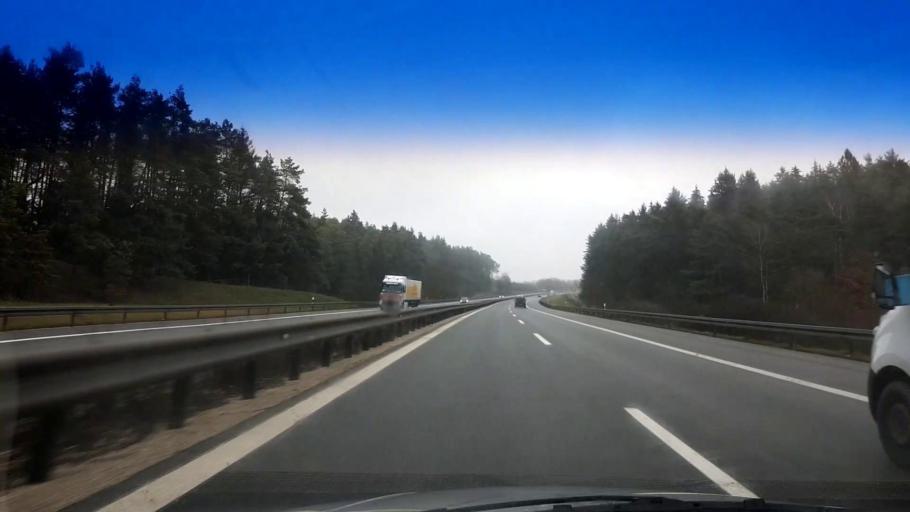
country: DE
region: Bavaria
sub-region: Upper Franconia
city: Stadelhofen
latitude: 49.9967
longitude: 11.1803
